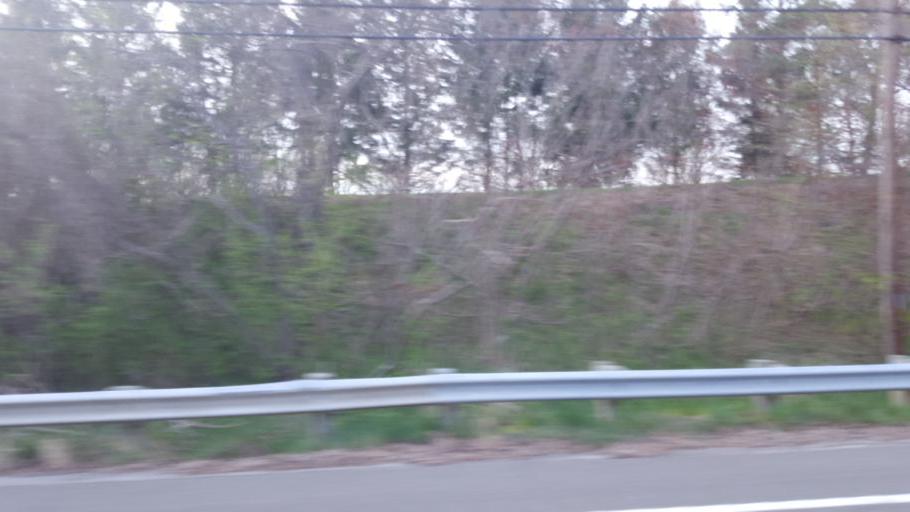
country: US
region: Ohio
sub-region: Lorain County
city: Vermilion
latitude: 41.3883
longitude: -82.4478
